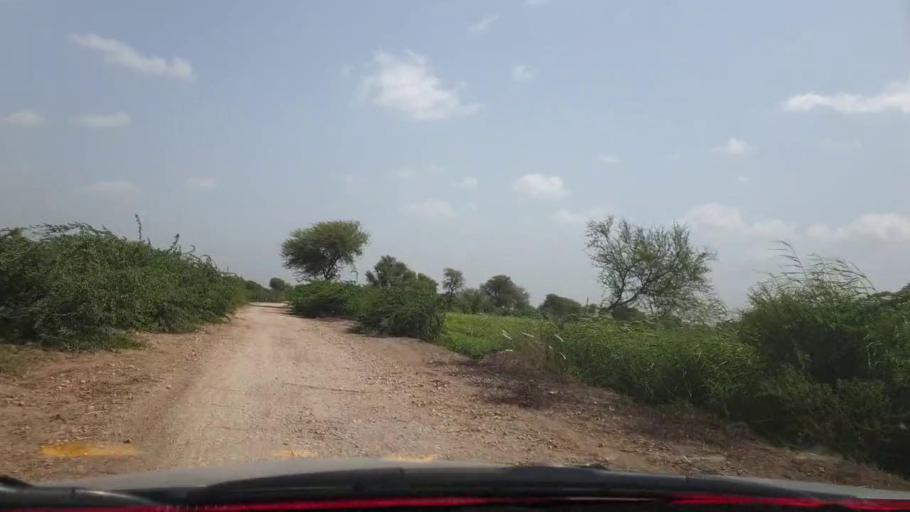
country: PK
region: Sindh
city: Talhar
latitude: 24.8894
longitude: 68.9066
